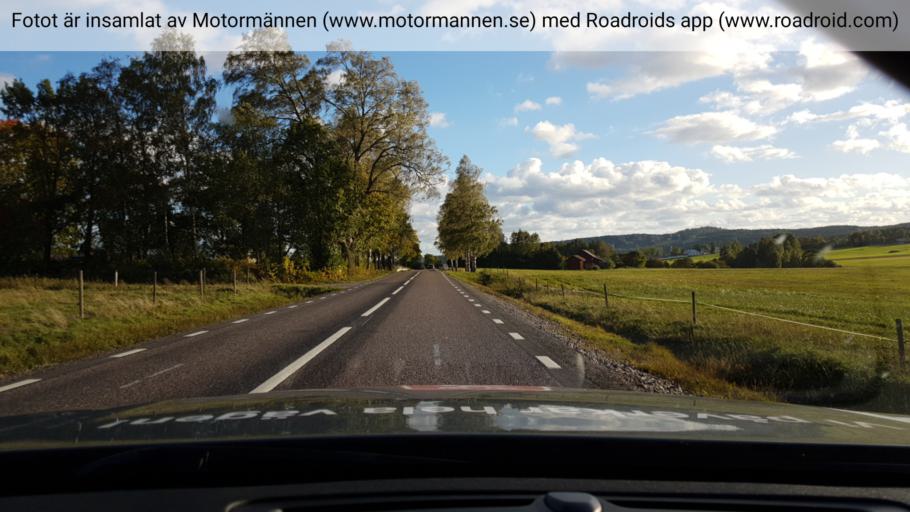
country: SE
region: Vaermland
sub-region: Karlstads Kommun
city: Molkom
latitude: 59.6932
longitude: 13.6819
